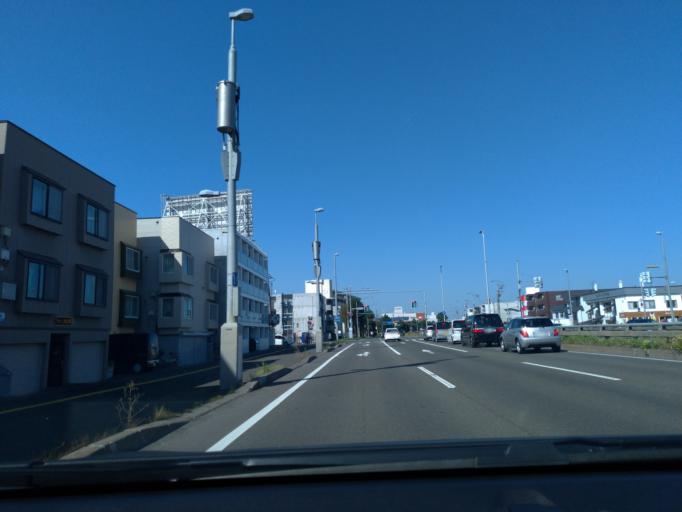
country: JP
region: Hokkaido
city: Sapporo
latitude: 43.1091
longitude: 141.3436
